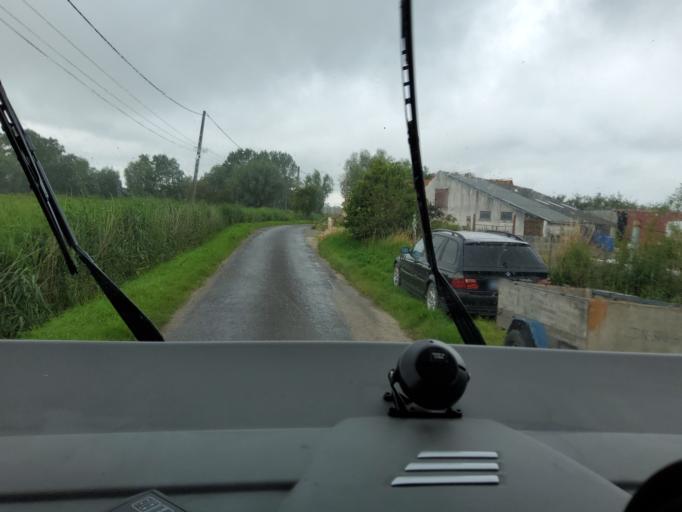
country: FR
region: Nord-Pas-de-Calais
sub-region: Departement du Pas-de-Calais
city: Sainte-Marie-Kerque
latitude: 50.9196
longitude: 2.1447
